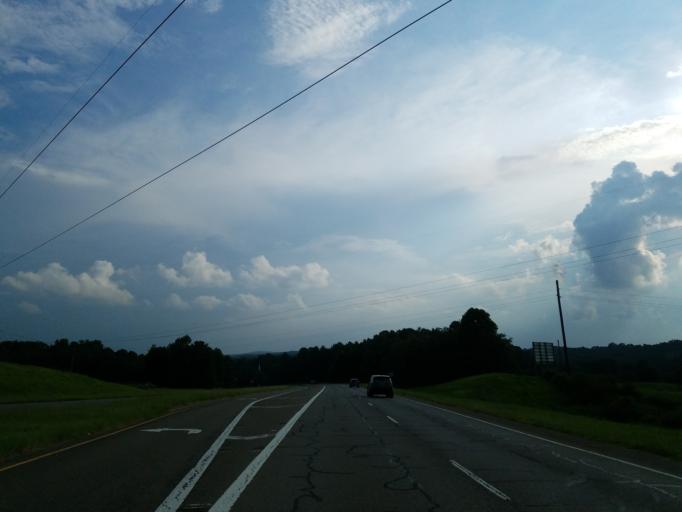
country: US
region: Georgia
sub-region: Gilmer County
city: Ellijay
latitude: 34.6268
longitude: -84.5107
